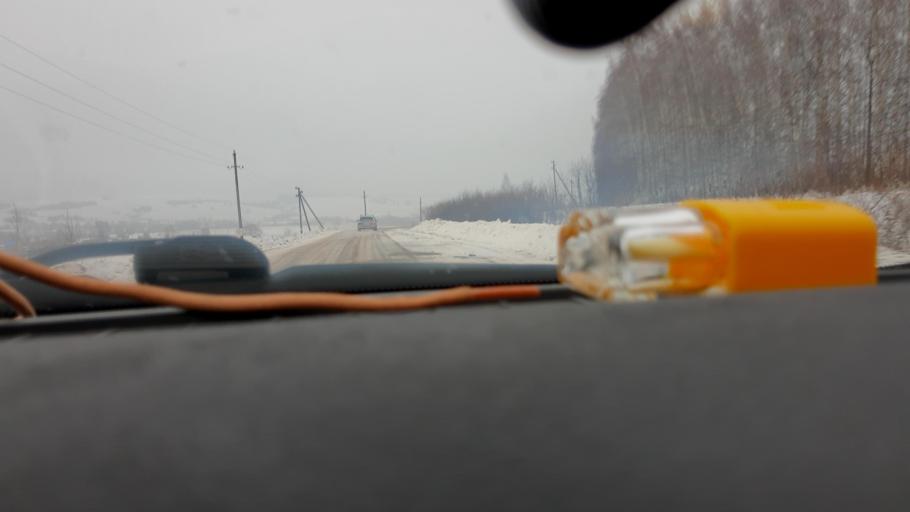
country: RU
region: Bashkortostan
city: Ulukulevo
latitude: 54.5578
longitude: 56.4351
